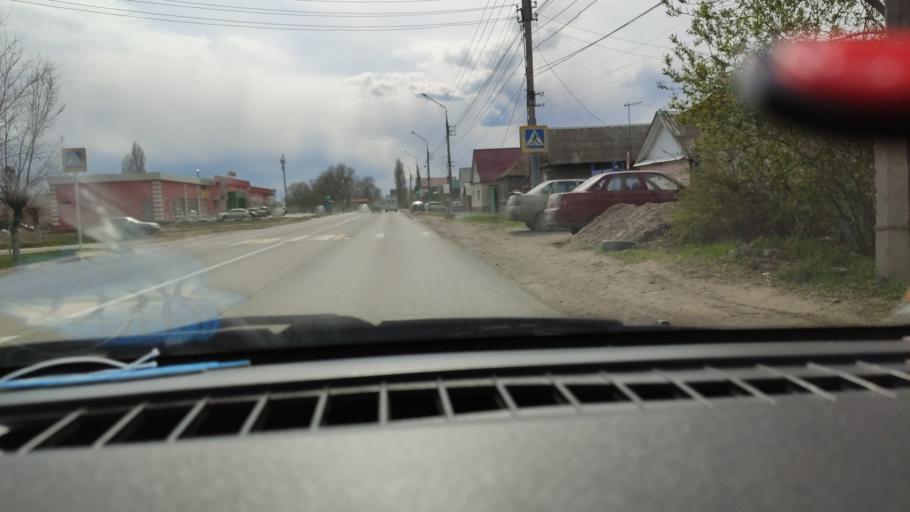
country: RU
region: Saratov
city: Privolzhskiy
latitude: 51.4245
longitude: 46.0461
